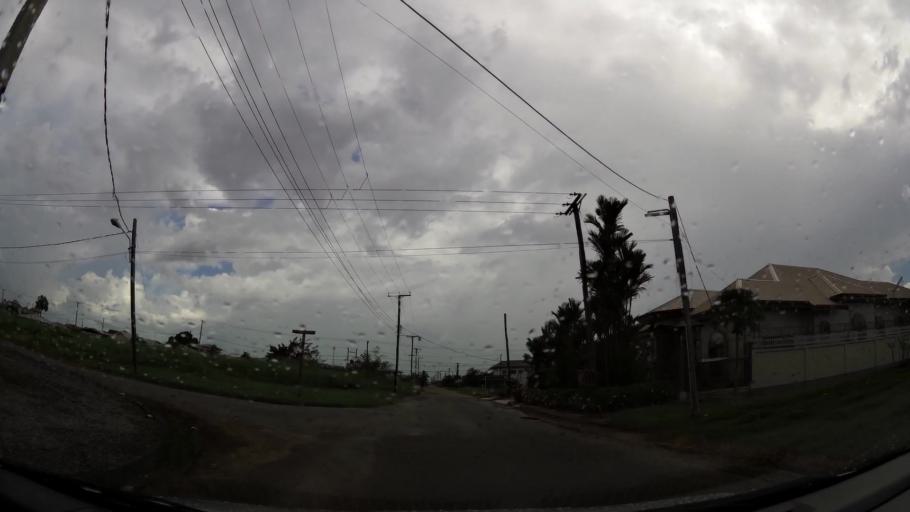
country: SR
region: Commewijne
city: Nieuw Amsterdam
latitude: 5.8605
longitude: -55.1158
